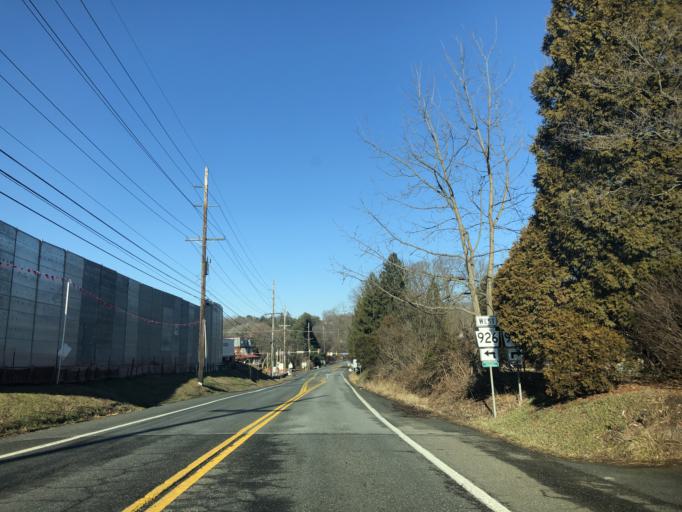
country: US
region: Pennsylvania
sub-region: Delaware County
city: Chester Heights
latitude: 39.9494
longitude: -75.5089
